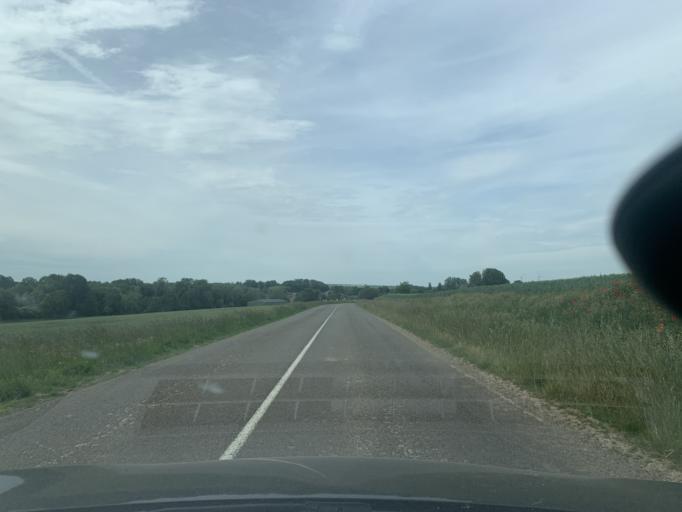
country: FR
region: Nord-Pas-de-Calais
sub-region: Departement du Nord
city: Marcoing
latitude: 50.1298
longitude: 3.1821
